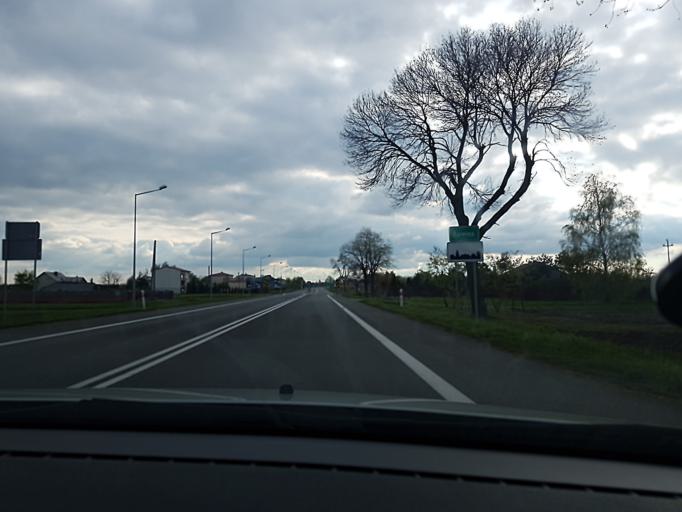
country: PL
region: Lodz Voivodeship
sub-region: powiat Lowicki
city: Lowicz
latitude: 52.1187
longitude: 19.9828
